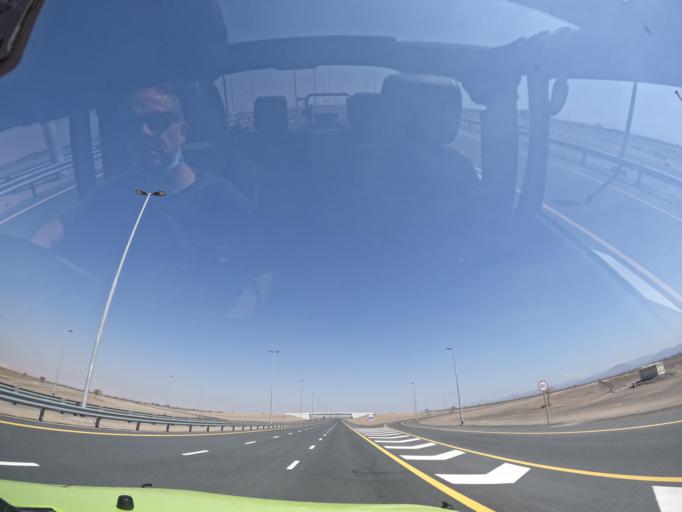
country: AE
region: Ash Shariqah
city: Adh Dhayd
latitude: 25.0435
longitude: 55.8914
